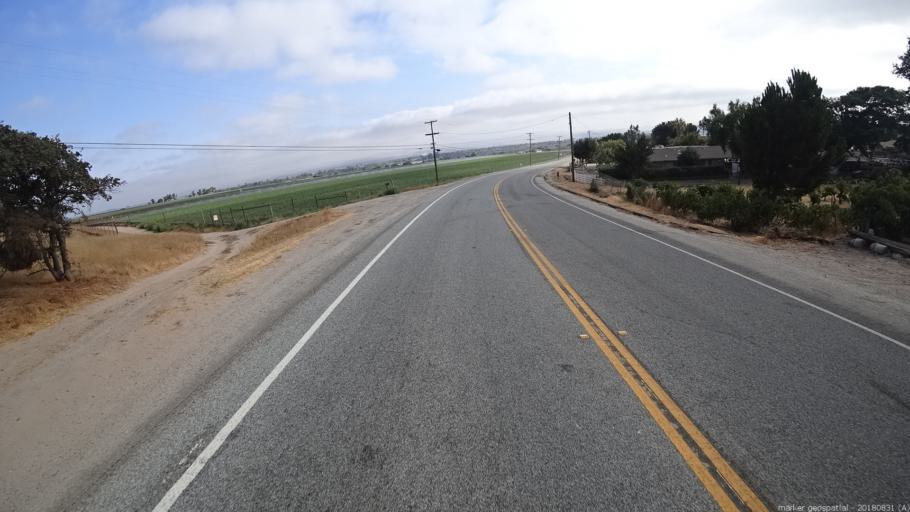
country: US
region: California
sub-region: Monterey County
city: King City
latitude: 36.1878
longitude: -121.1499
